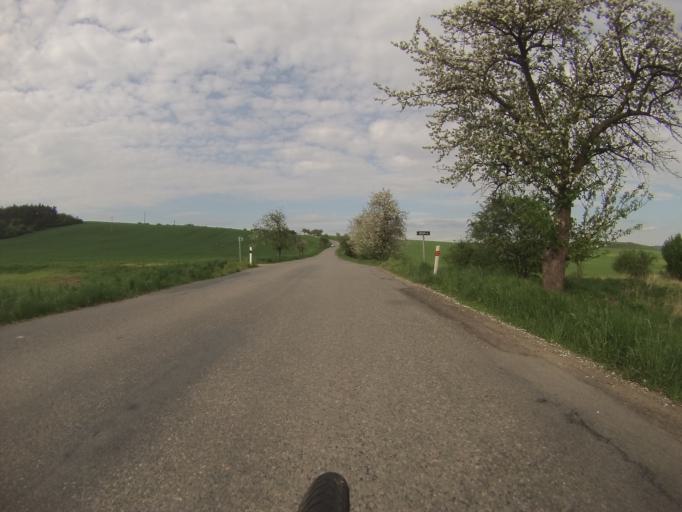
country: CZ
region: South Moravian
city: Cebin
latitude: 49.2967
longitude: 16.4565
